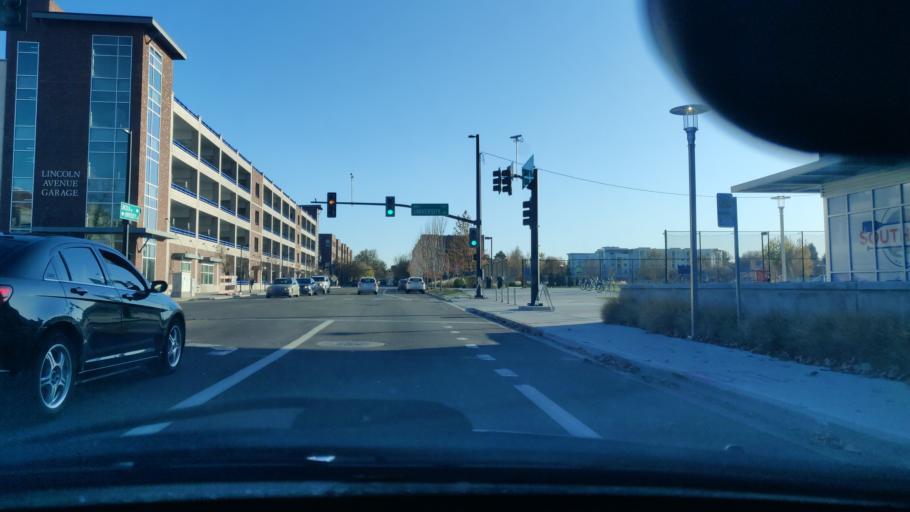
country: US
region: Idaho
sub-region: Ada County
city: Boise
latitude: 43.6013
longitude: -116.2024
